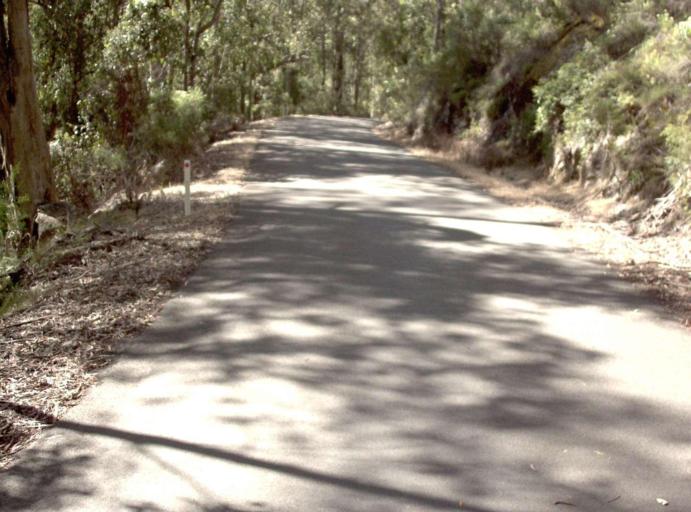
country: AU
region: Victoria
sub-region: East Gippsland
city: Lakes Entrance
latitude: -37.4136
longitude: 148.1197
